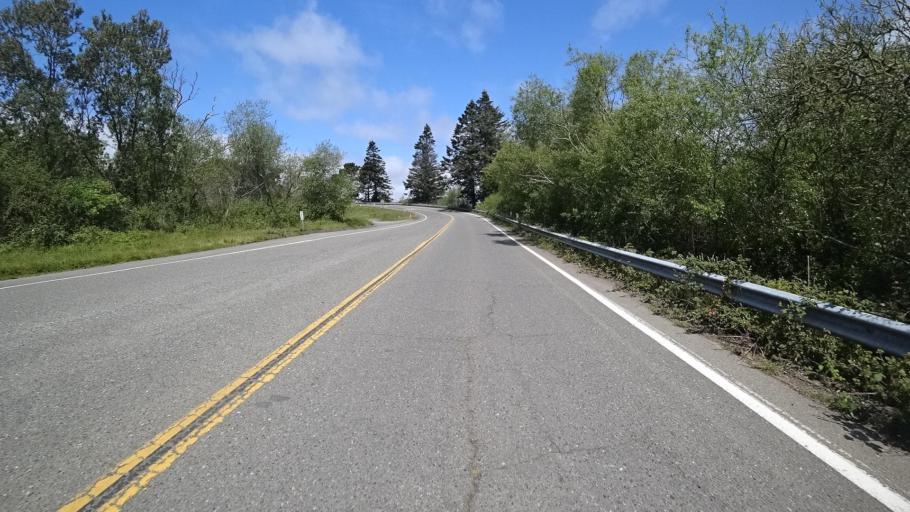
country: US
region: California
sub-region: Humboldt County
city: Humboldt Hill
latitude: 40.6709
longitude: -124.2005
